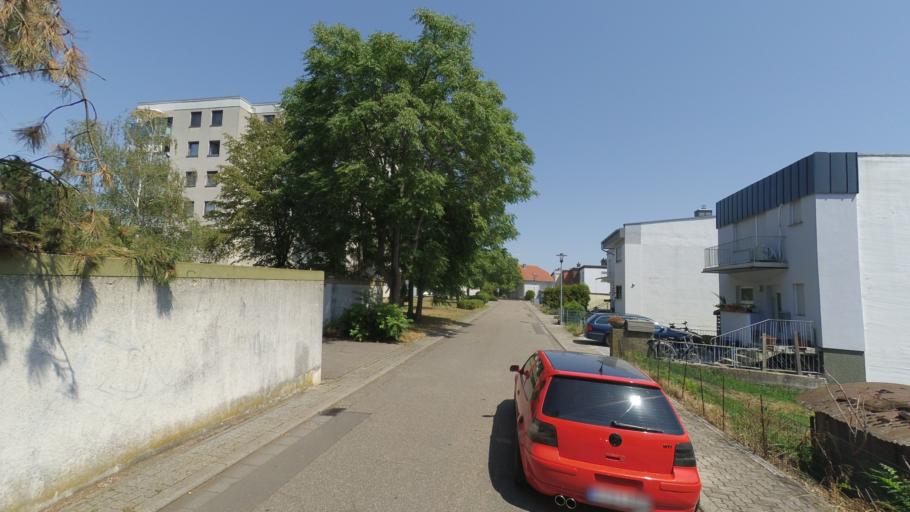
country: DE
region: Rheinland-Pfalz
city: Schifferstadt
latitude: 49.3905
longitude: 8.3824
